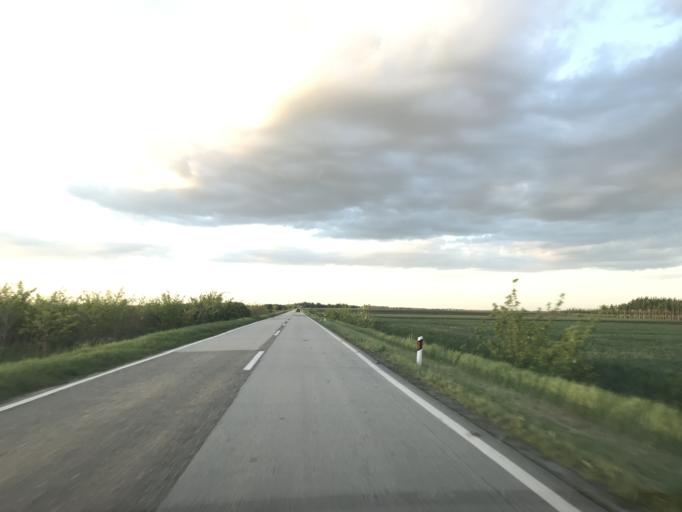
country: RS
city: Banatsko Karadordevo
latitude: 45.5995
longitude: 20.5631
